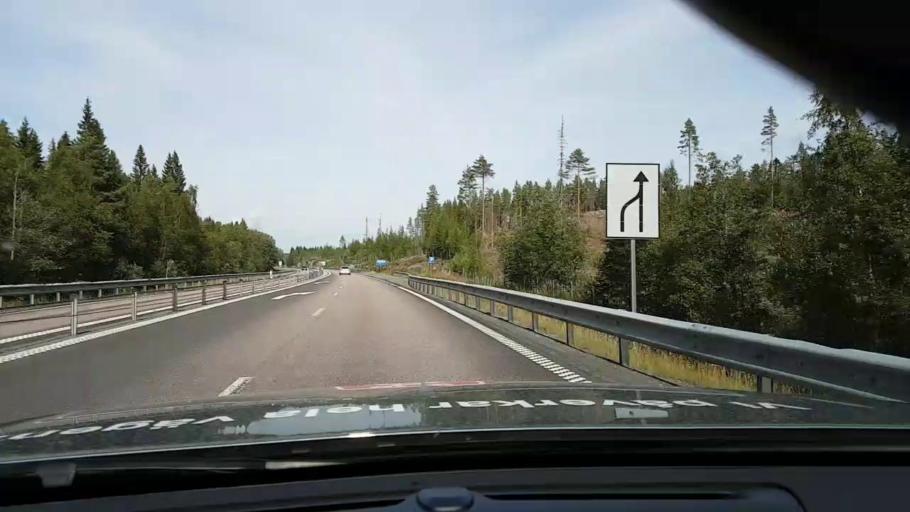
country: SE
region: Vaesternorrland
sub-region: OErnskoeldsviks Kommun
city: Husum
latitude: 63.4304
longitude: 19.2090
